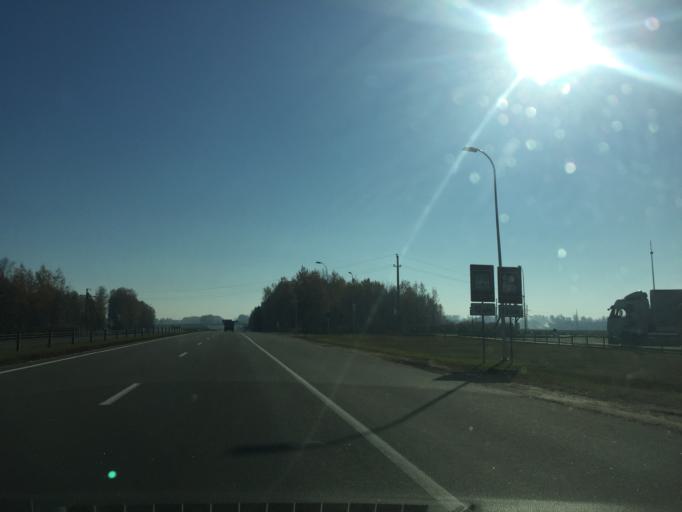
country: BY
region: Mogilev
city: Buynichy
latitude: 53.9532
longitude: 30.2131
